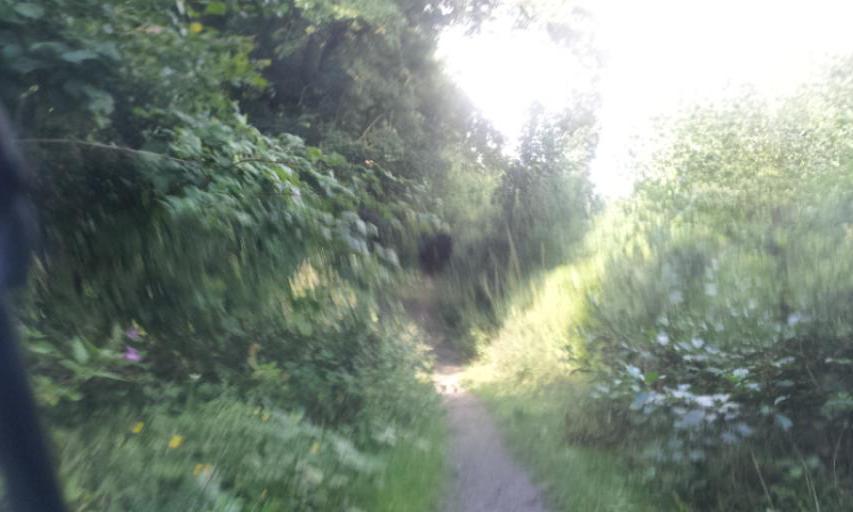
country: GB
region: England
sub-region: Kent
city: West Malling
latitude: 51.2995
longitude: 0.4165
